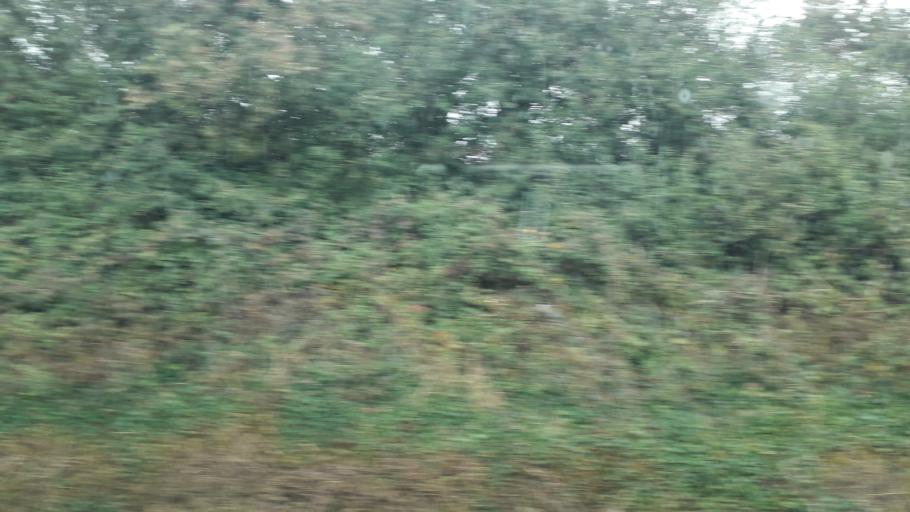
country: IE
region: Leinster
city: Donabate
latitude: 53.4814
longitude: -6.1520
